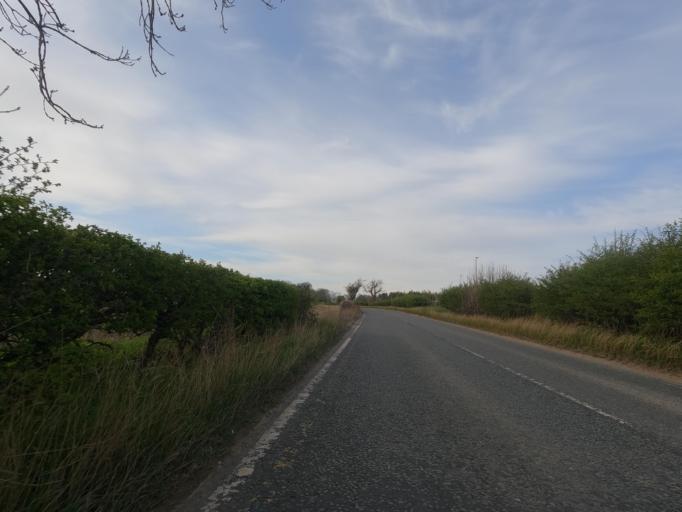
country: GB
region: England
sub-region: Newcastle upon Tyne
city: Dinnington
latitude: 55.0293
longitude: -1.6647
